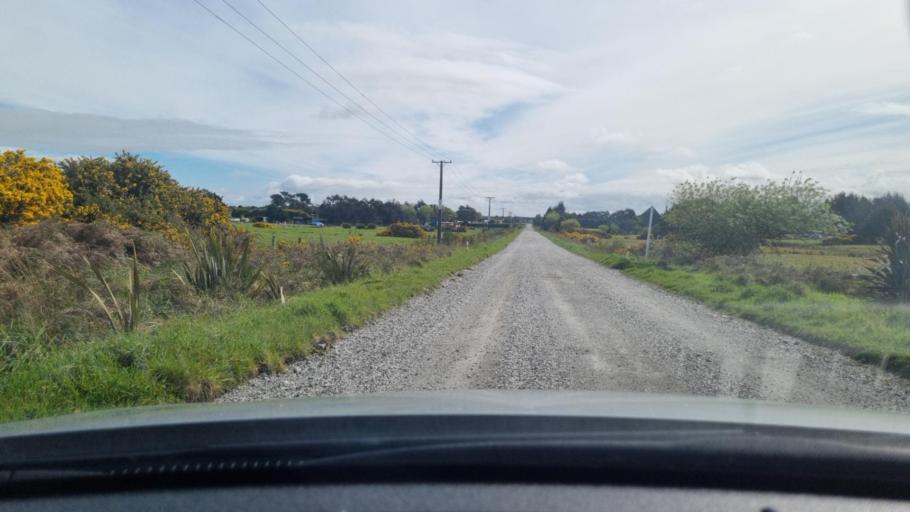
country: NZ
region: Southland
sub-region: Invercargill City
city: Invercargill
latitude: -46.4507
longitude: 168.3929
